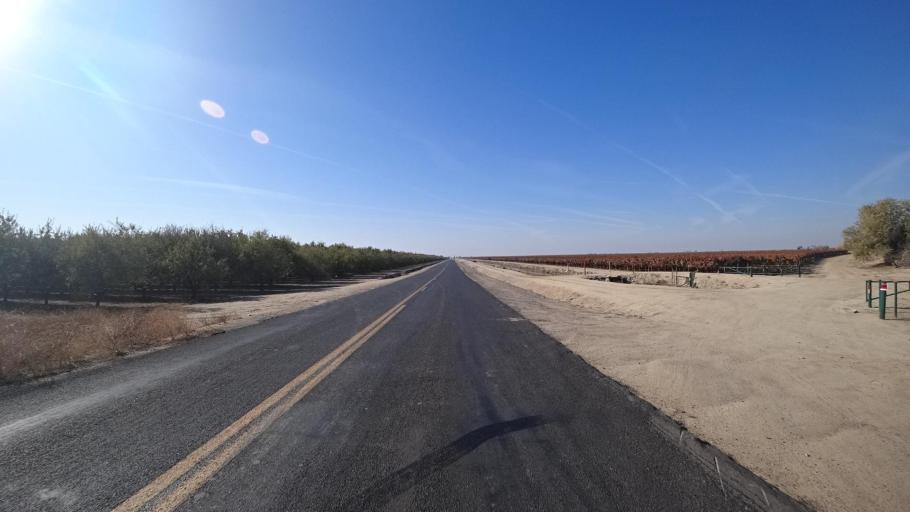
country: US
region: California
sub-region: Kern County
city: McFarland
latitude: 35.6453
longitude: -119.2794
